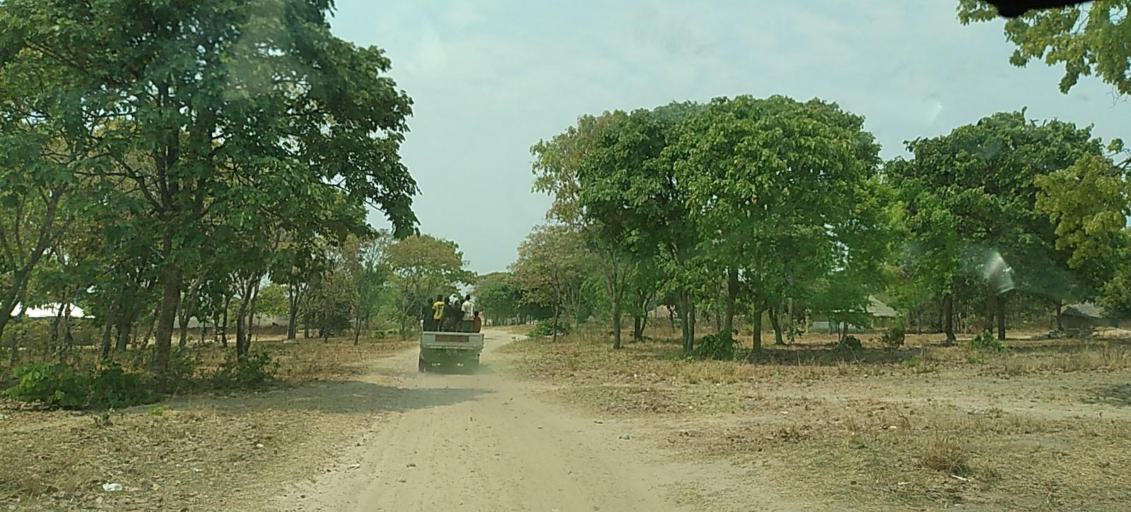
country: ZM
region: North-Western
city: Kabompo
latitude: -13.4893
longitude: 24.4622
